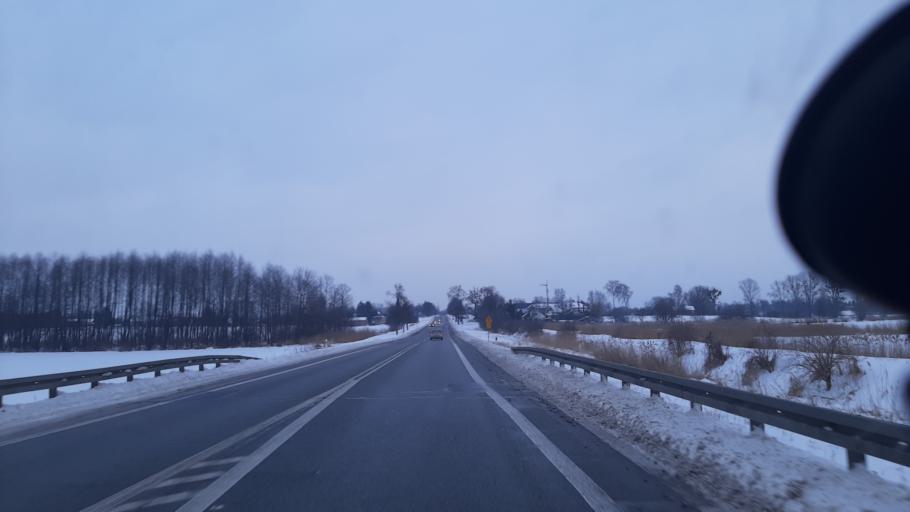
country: PL
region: Lublin Voivodeship
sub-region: Powiat lubelski
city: Garbow
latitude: 51.3614
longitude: 22.3078
